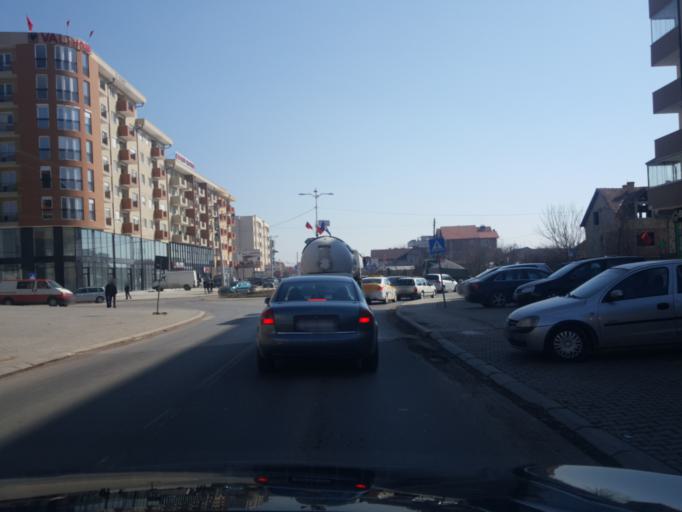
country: XK
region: Mitrovica
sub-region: Vushtrri
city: Vushtrri
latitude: 42.8271
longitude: 20.9697
